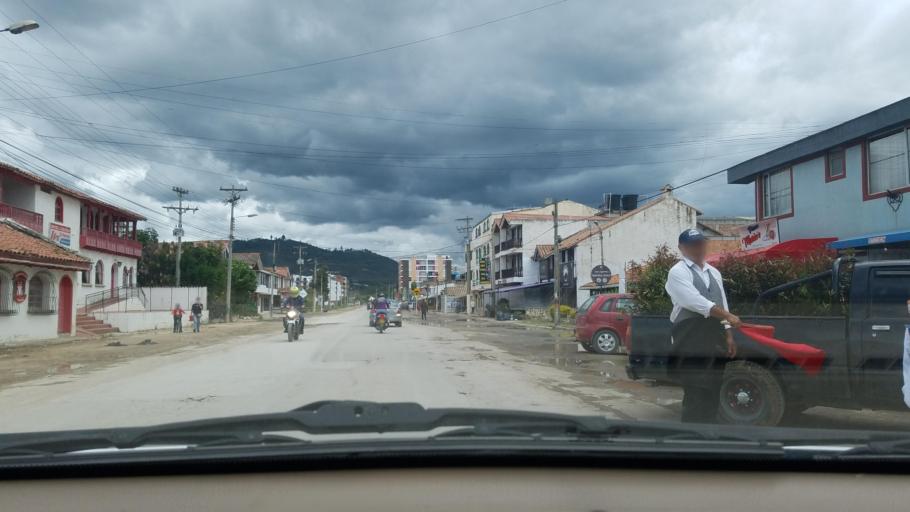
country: CO
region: Boyaca
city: Paipa
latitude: 5.7728
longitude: -73.1162
